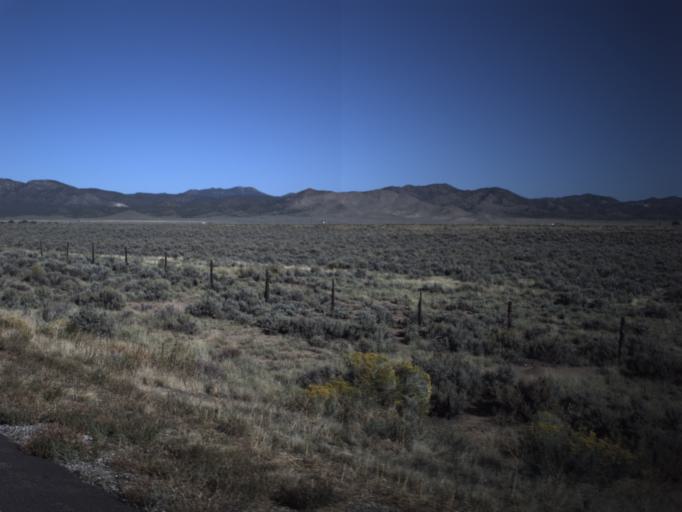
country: US
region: Utah
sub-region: Washington County
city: Enterprise
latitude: 37.7868
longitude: -113.8768
